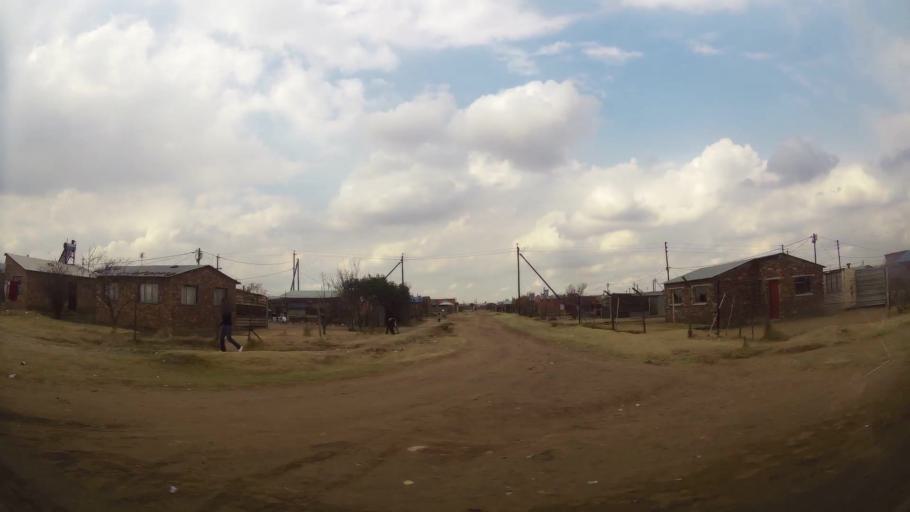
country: ZA
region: Orange Free State
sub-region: Fezile Dabi District Municipality
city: Sasolburg
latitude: -26.8614
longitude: 27.8920
